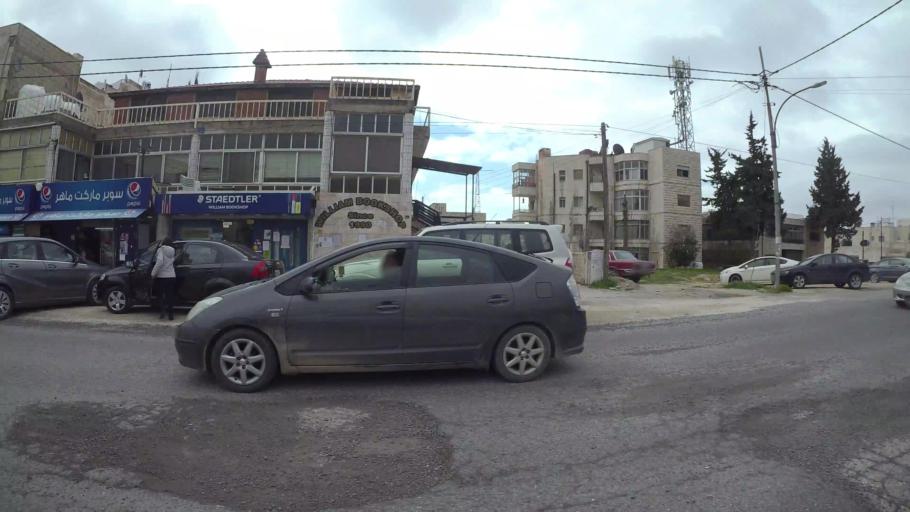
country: JO
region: Amman
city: Wadi as Sir
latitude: 31.9654
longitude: 35.8541
